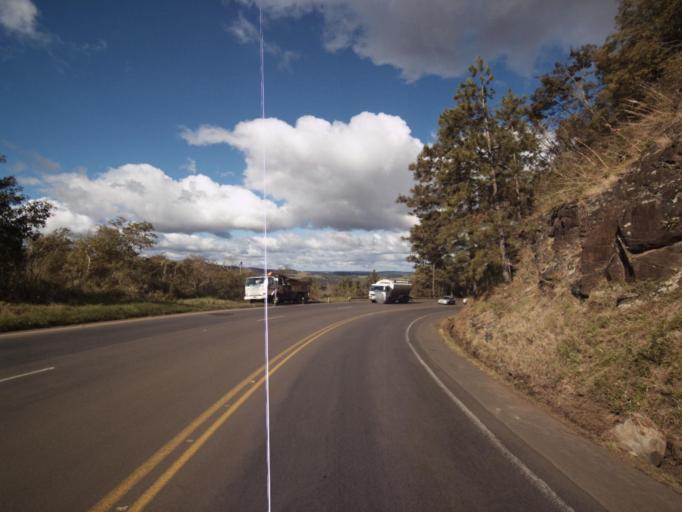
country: BR
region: Santa Catarina
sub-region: Joacaba
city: Joacaba
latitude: -26.9789
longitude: -51.7570
